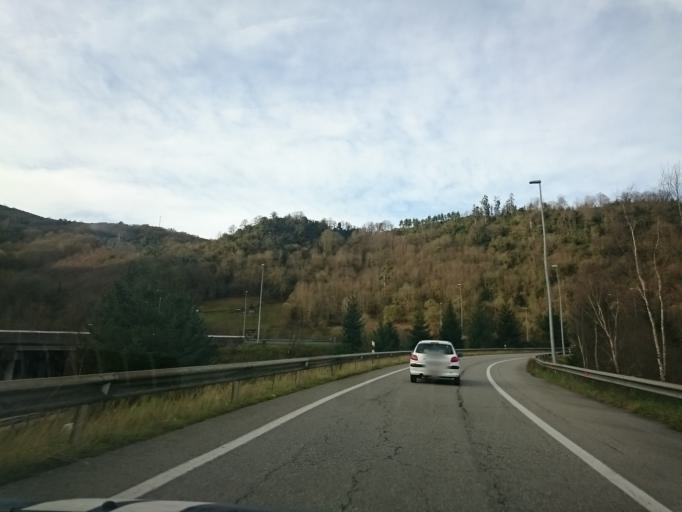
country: ES
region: Asturias
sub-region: Province of Asturias
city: Castandiello
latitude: 43.3019
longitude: -5.8399
